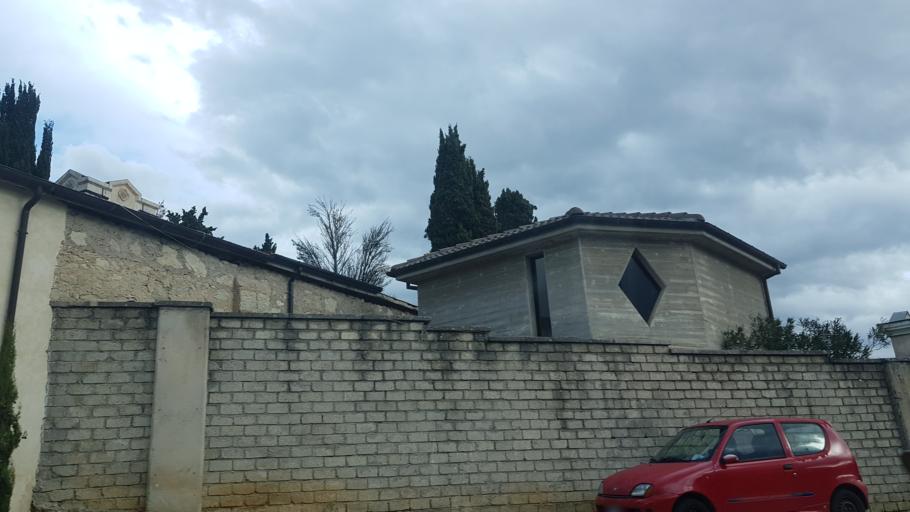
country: IT
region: Abruzzo
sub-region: Provincia dell' Aquila
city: L'Aquila
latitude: 42.3506
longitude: 13.4111
